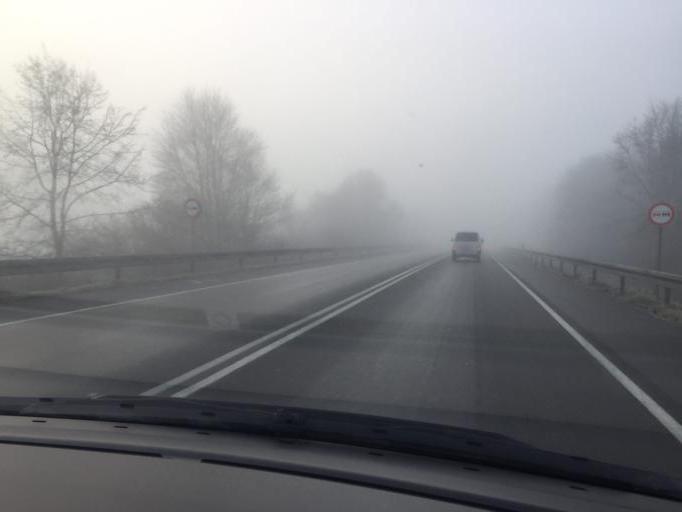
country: DE
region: Baden-Wuerttemberg
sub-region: Freiburg Region
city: Donaueschingen
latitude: 47.9441
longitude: 8.5196
